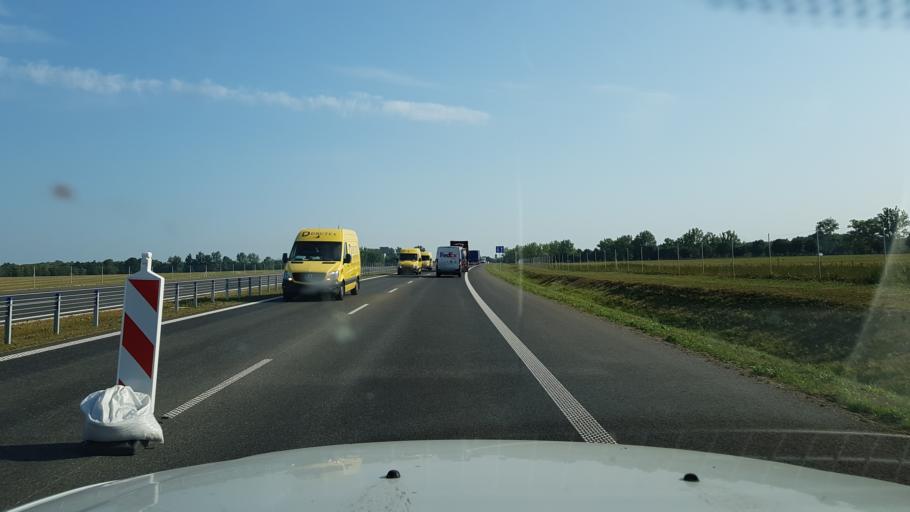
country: PL
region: West Pomeranian Voivodeship
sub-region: Powiat gryficki
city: Ploty
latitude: 53.7770
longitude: 15.2402
